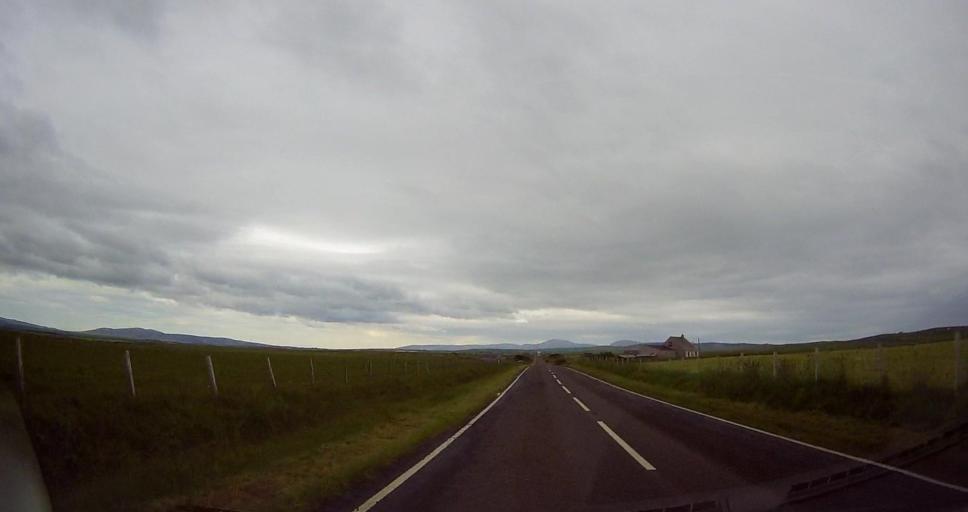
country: GB
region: Scotland
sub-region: Orkney Islands
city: Stromness
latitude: 59.0745
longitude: -3.2786
